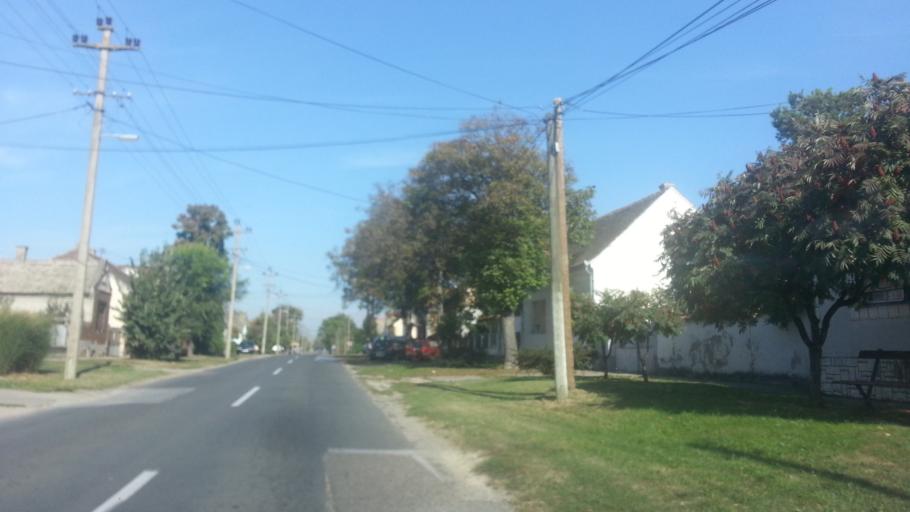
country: RS
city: Belegis
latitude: 45.0150
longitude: 20.3267
